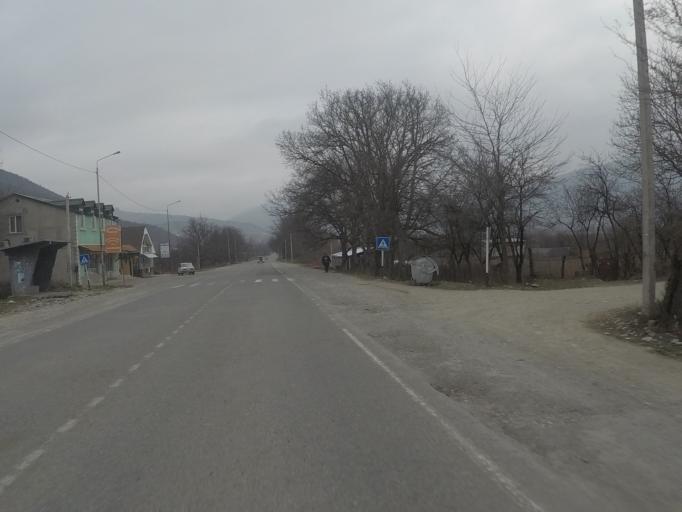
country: GE
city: Zhinvali
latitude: 42.0805
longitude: 44.7528
